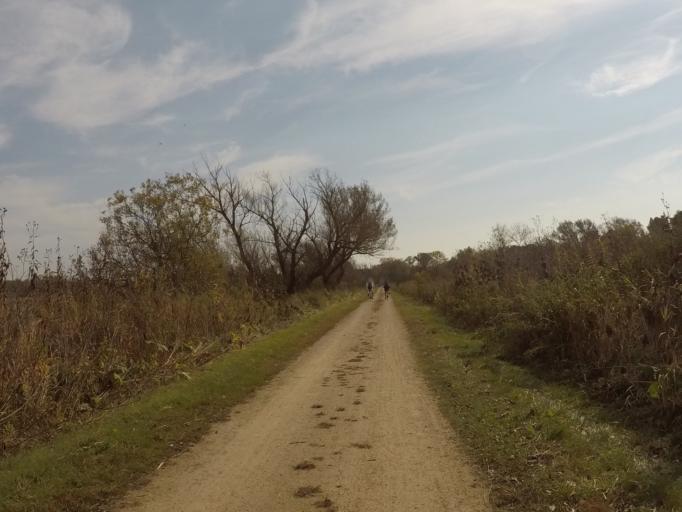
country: US
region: Wisconsin
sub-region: Dane County
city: Cross Plains
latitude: 43.0259
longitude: -89.6305
